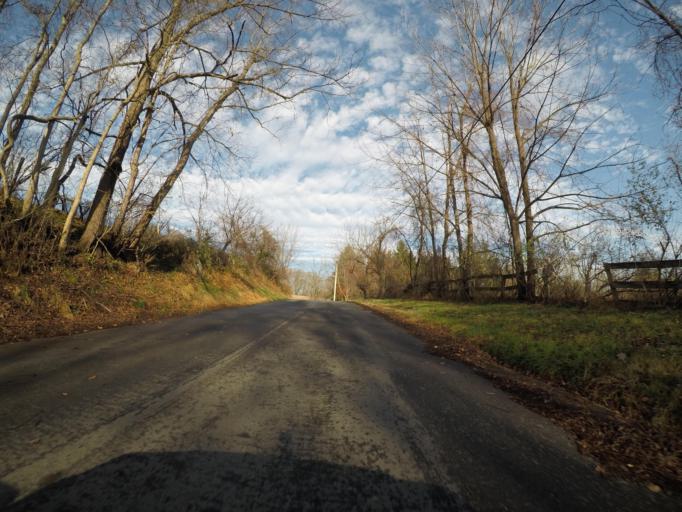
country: US
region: Maryland
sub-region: Carroll County
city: Hampstead
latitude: 39.5787
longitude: -76.8151
